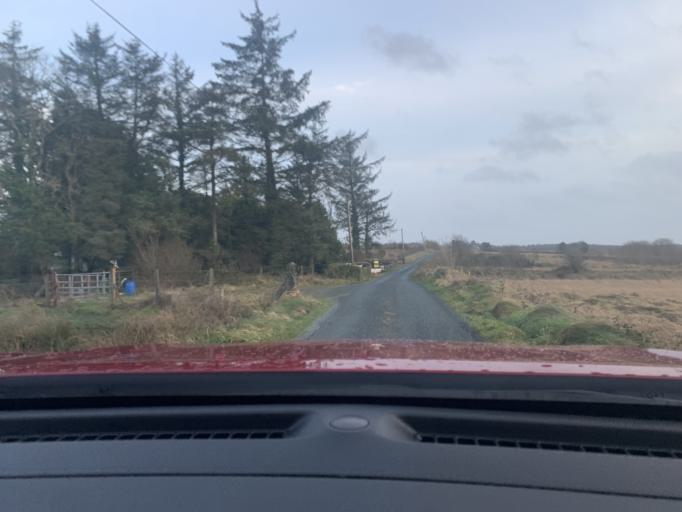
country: IE
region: Connaught
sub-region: Roscommon
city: Ballaghaderreen
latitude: 53.9571
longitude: -8.5341
